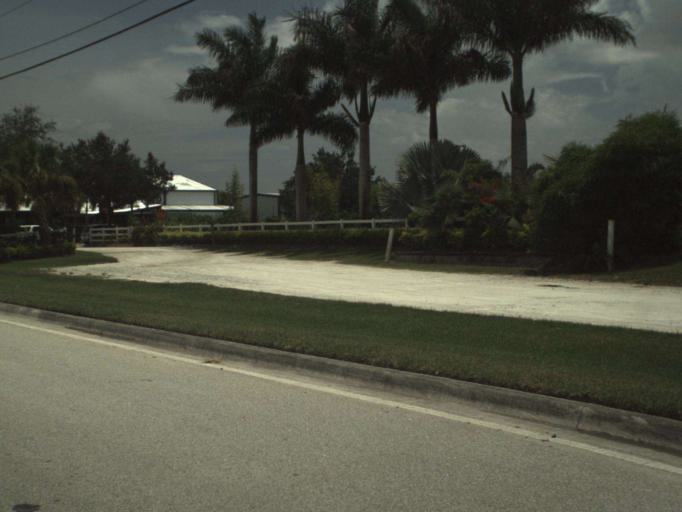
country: US
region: Florida
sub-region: Saint Lucie County
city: White City
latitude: 27.3743
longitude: -80.3338
